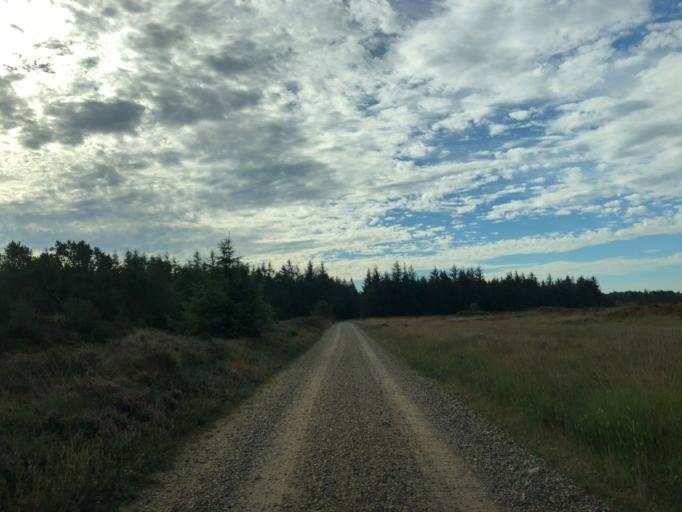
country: DK
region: Central Jutland
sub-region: Holstebro Kommune
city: Ulfborg
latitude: 56.1811
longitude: 8.3519
